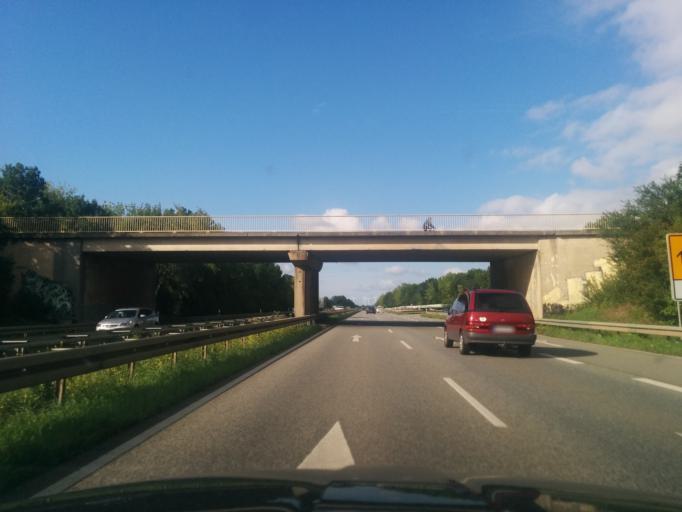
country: DE
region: Saxony-Anhalt
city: Halle Neustadt
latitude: 51.4738
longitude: 11.9390
